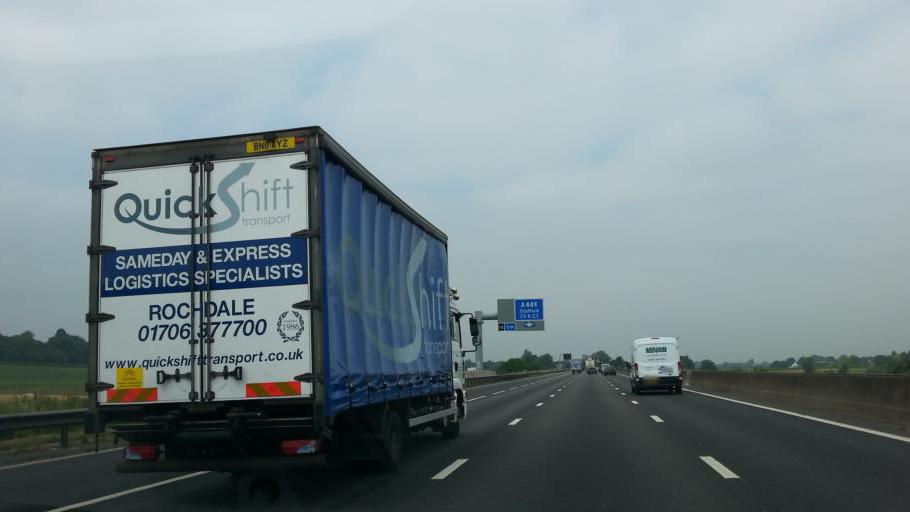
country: GB
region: England
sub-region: Staffordshire
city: Penkridge
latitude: 52.7520
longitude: -2.1009
